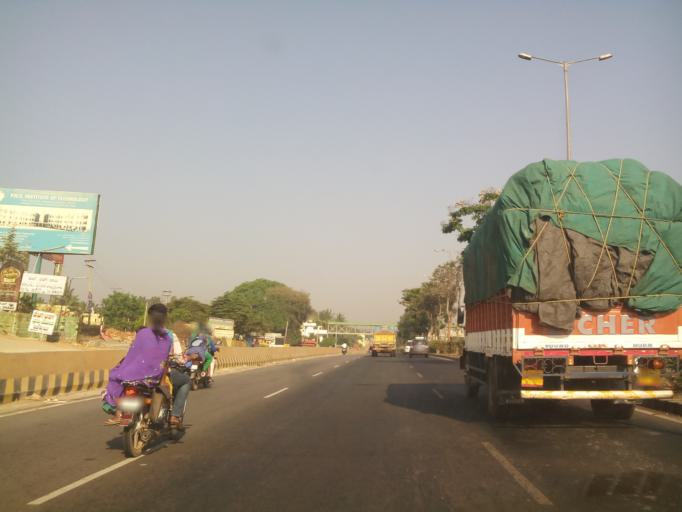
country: IN
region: Karnataka
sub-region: Bangalore Rural
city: Nelamangala
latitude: 13.0873
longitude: 77.4076
